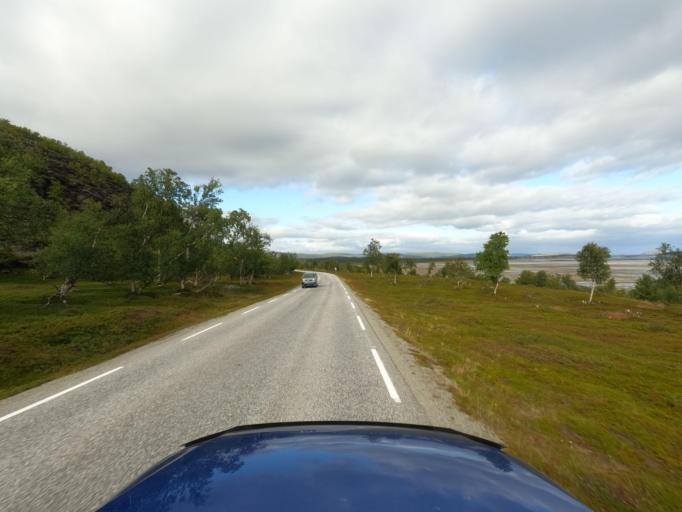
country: NO
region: Finnmark Fylke
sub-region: Porsanger
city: Lakselv
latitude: 70.1399
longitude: 24.9116
